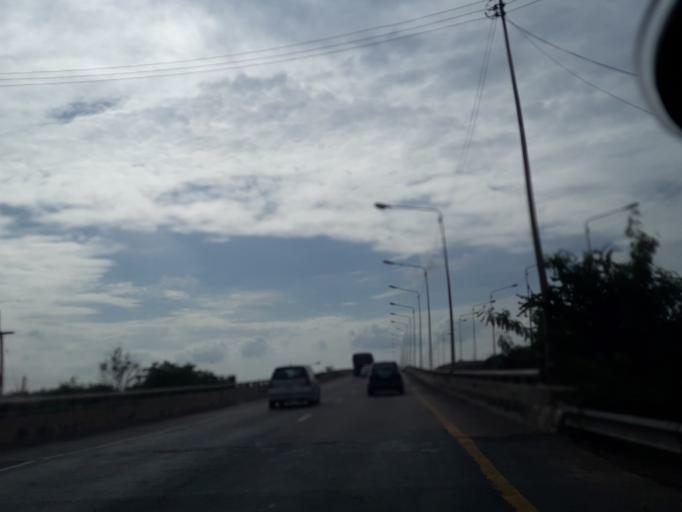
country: TH
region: Sara Buri
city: Saraburi
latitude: 14.5444
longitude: 100.9489
